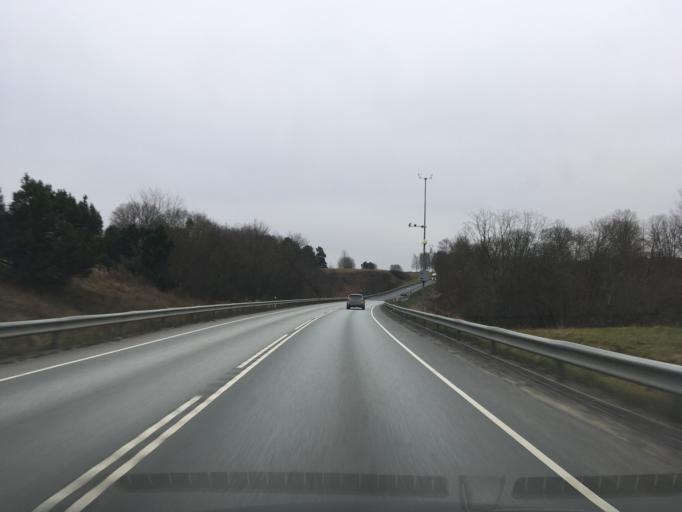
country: EE
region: Ida-Virumaa
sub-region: Aseri vald
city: Aseri
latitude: 59.4334
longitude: 26.7058
